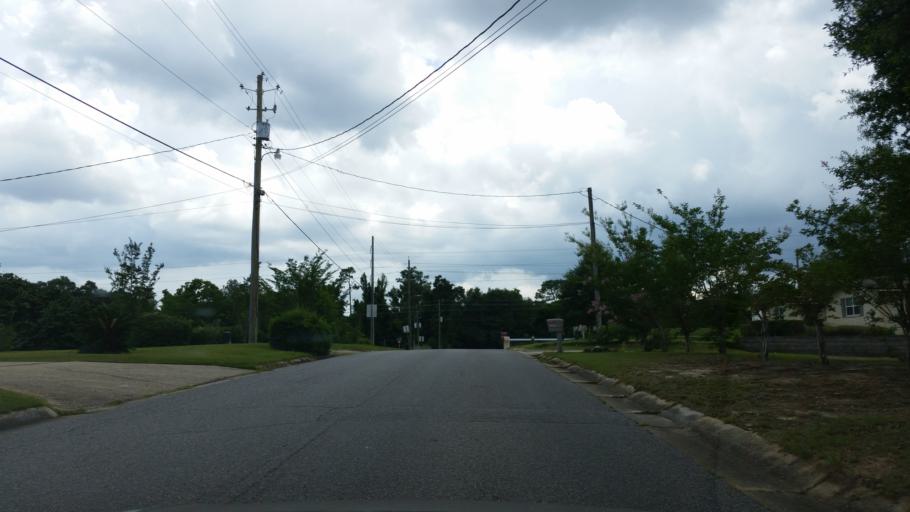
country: US
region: Florida
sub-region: Escambia County
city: Ferry Pass
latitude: 30.5337
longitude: -87.2311
